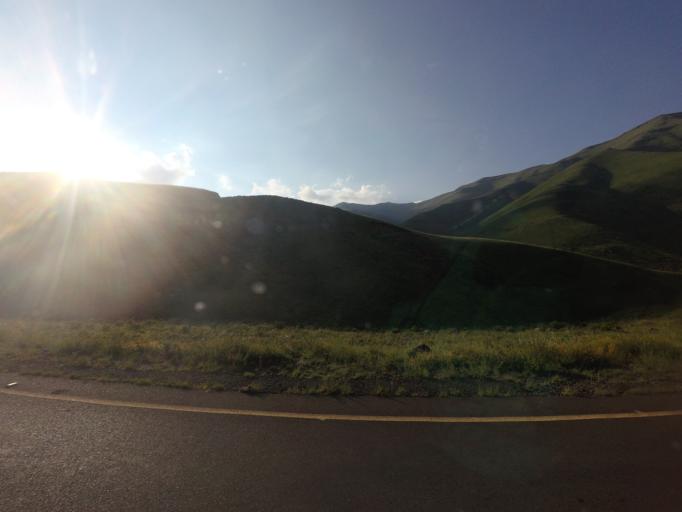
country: LS
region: Butha-Buthe
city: Butha-Buthe
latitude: -29.1125
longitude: 28.4569
